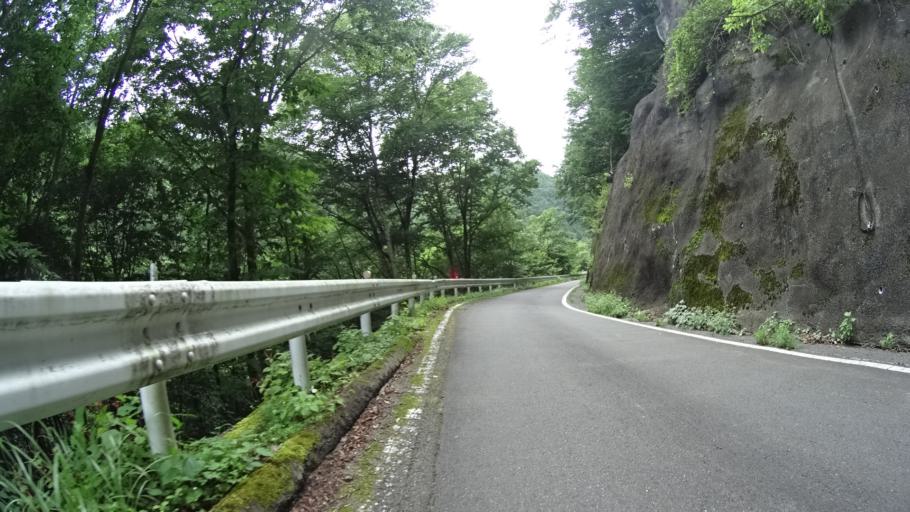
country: JP
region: Nagano
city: Saku
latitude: 36.0670
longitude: 138.6561
